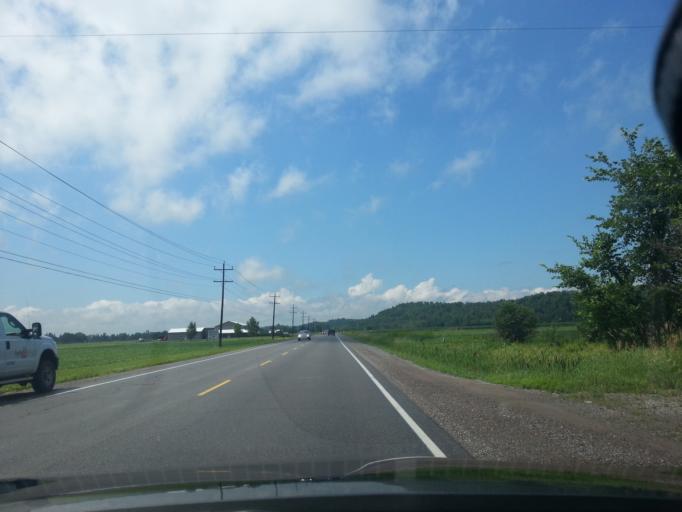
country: CA
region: Ontario
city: Renfrew
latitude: 45.4924
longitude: -76.7353
